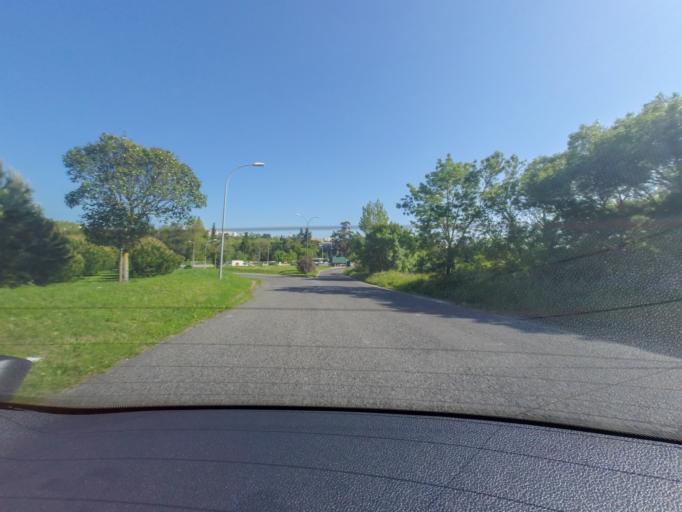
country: PT
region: Lisbon
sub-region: Sintra
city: Queluz
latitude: 38.7468
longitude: -9.2579
